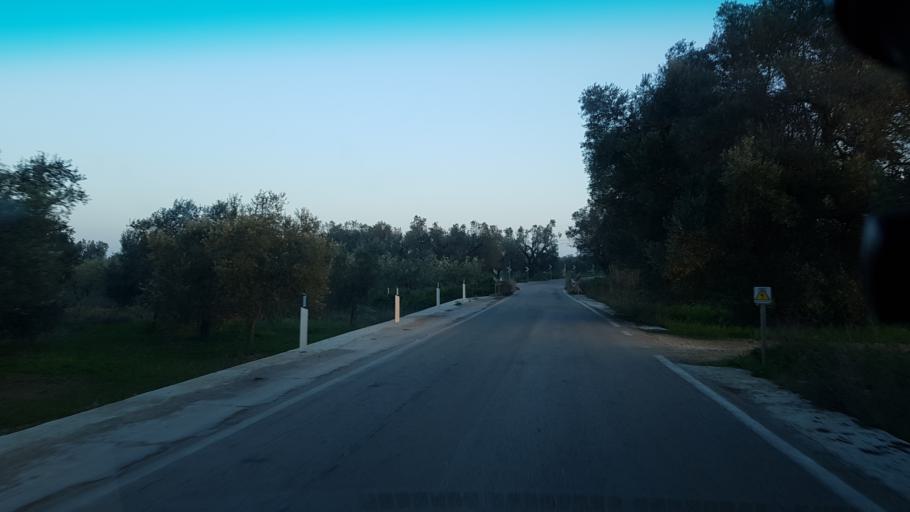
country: IT
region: Apulia
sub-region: Provincia di Brindisi
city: Mesagne
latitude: 40.6087
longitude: 17.7906
